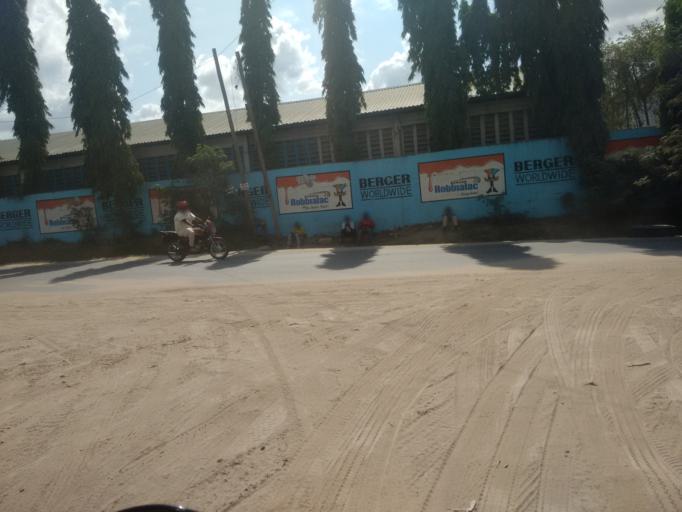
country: TZ
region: Dar es Salaam
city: Dar es Salaam
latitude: -6.8380
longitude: 39.2695
